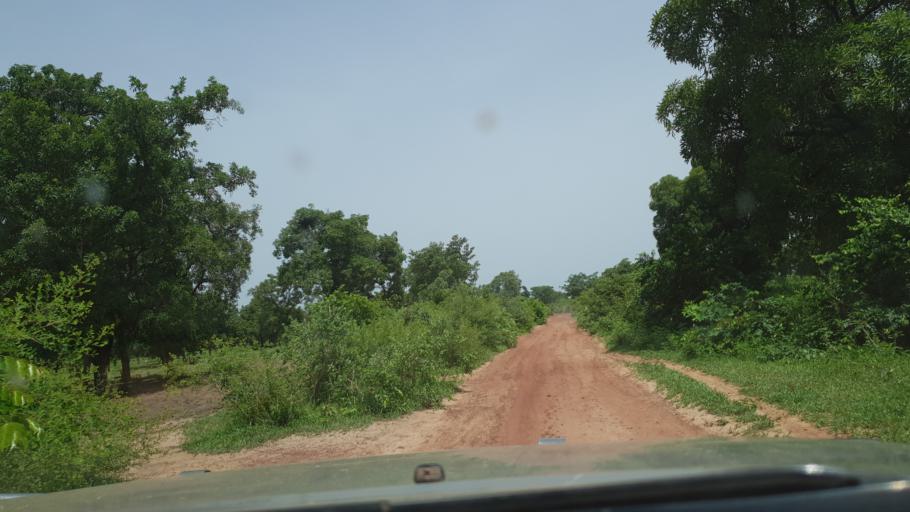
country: ML
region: Koulikoro
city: Koulikoro
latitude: 12.6642
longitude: -7.2143
